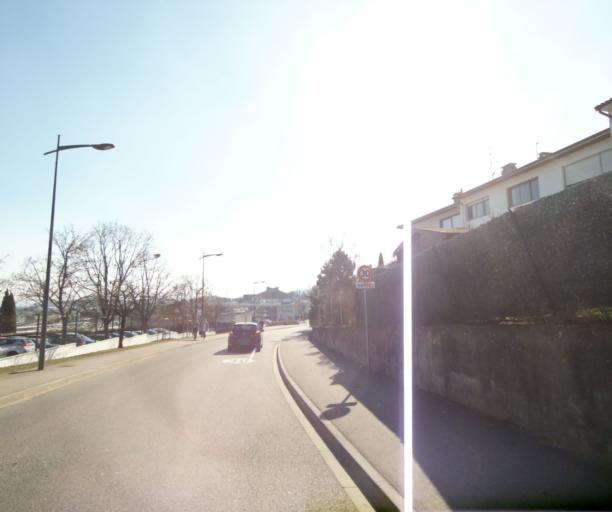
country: FR
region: Lorraine
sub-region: Departement de Meurthe-et-Moselle
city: Vandoeuvre-les-Nancy
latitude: 48.6553
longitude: 6.1765
